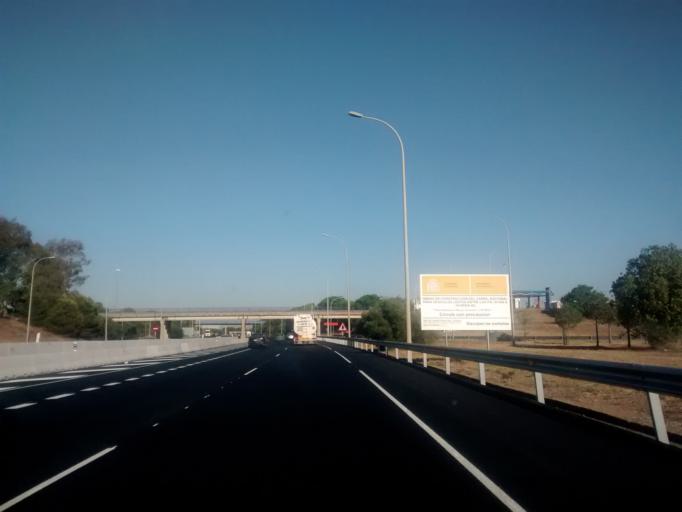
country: ES
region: Andalusia
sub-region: Provincia de Sevilla
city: Benacazon
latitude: 37.3608
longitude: -6.1983
